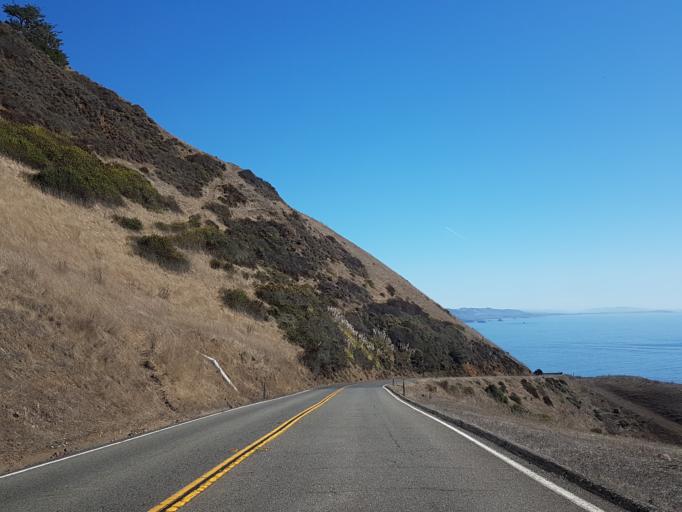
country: US
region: California
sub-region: Sonoma County
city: Monte Rio
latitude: 38.4943
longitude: -123.1981
